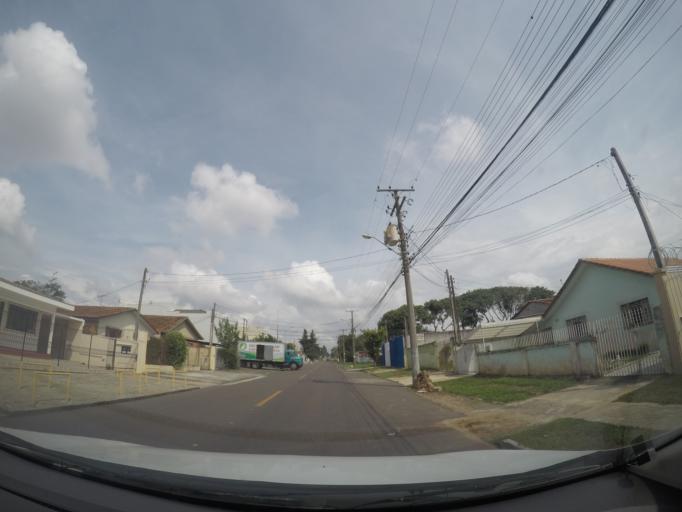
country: BR
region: Parana
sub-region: Curitiba
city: Curitiba
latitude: -25.4792
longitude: -49.2640
